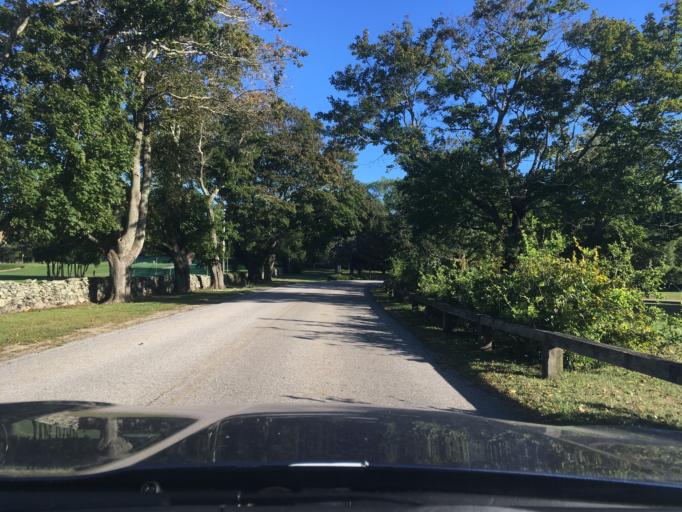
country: US
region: Rhode Island
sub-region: Kent County
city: East Greenwich
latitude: 41.6592
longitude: -71.4297
